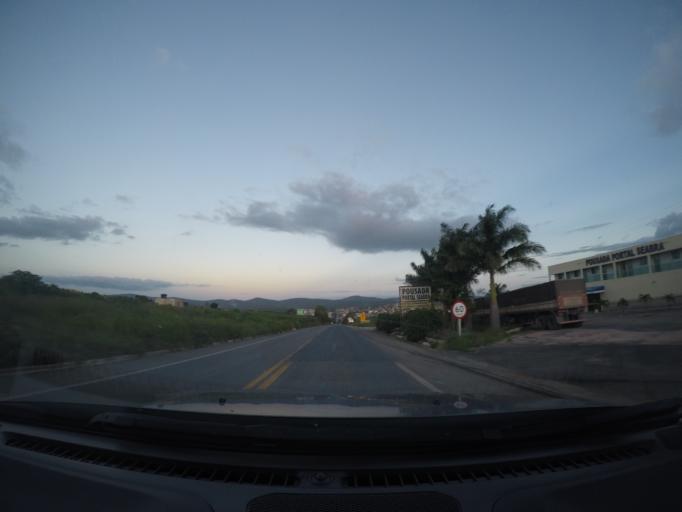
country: BR
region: Bahia
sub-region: Seabra
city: Seabra
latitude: -12.4290
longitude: -41.7885
